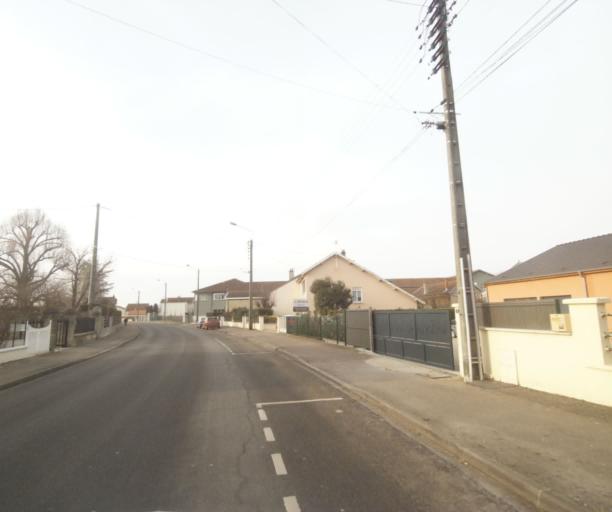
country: FR
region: Champagne-Ardenne
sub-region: Departement de la Haute-Marne
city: Saint-Dizier
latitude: 48.6338
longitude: 4.9368
